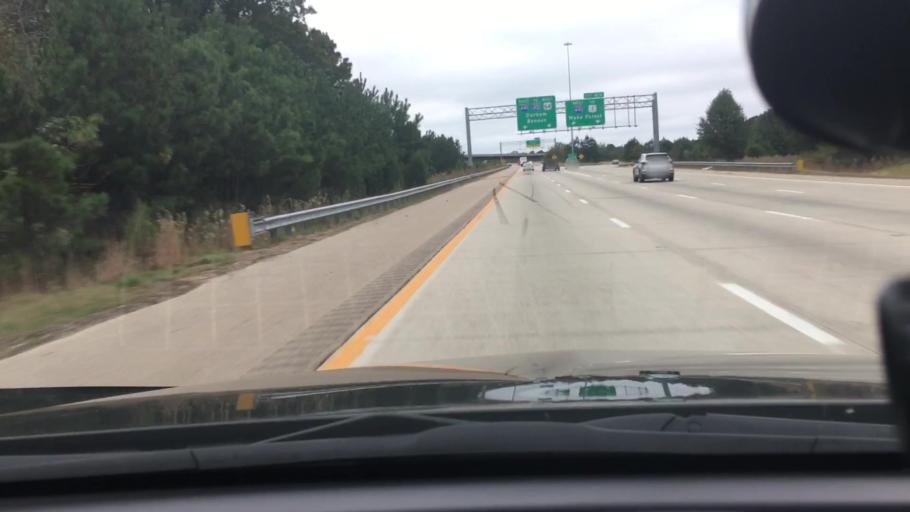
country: US
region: North Carolina
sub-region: Wake County
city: Raleigh
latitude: 35.7805
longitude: -78.5682
